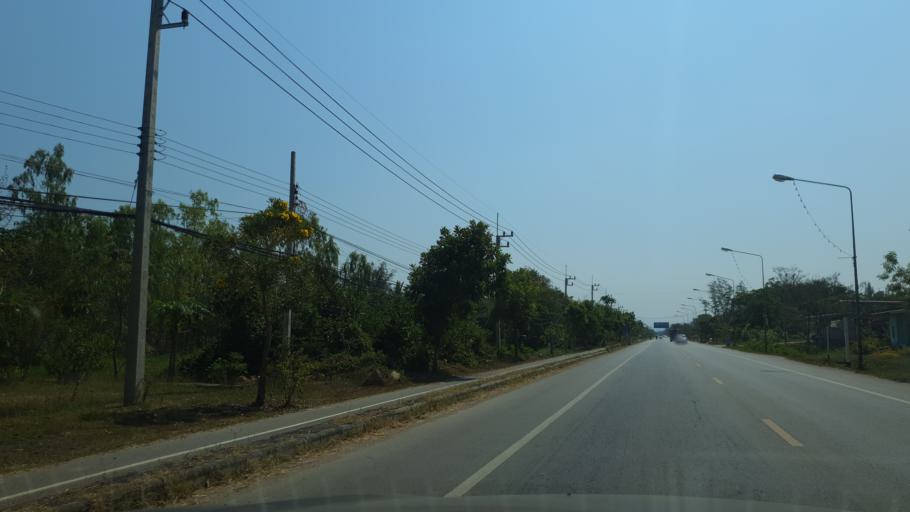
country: TH
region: Prachuap Khiri Khan
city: Pran Buri
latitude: 12.3615
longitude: 99.9357
